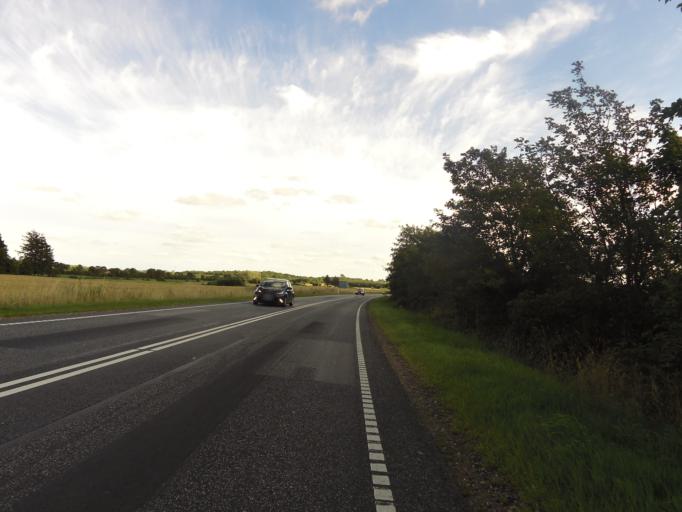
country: DK
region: South Denmark
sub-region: Tonder Kommune
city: Toftlund
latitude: 55.2068
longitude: 9.0477
